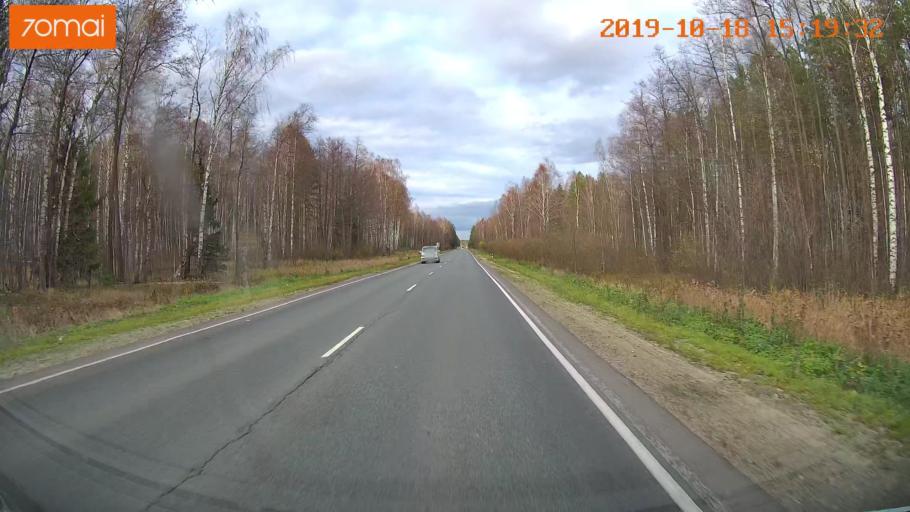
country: RU
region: Vladimir
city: Anopino
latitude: 55.6745
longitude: 40.7384
